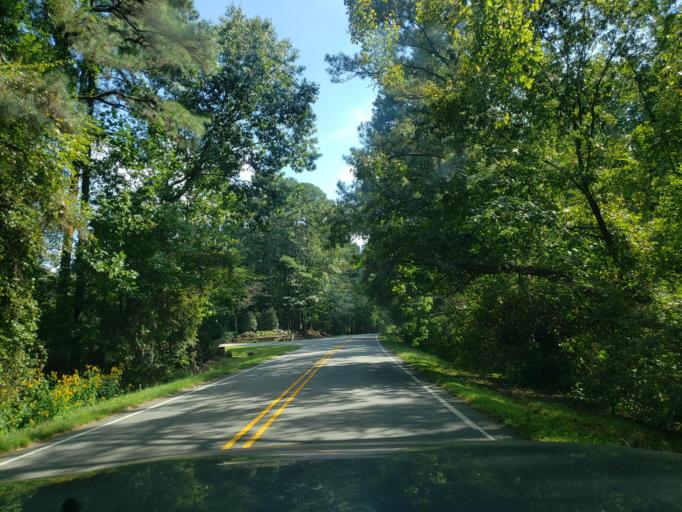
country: US
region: North Carolina
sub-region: Wake County
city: West Raleigh
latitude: 35.9346
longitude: -78.6933
